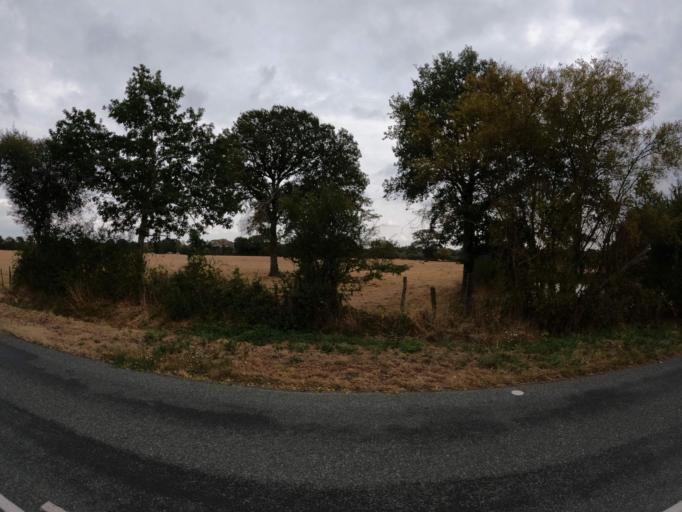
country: FR
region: Pays de la Loire
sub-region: Departement de Maine-et-Loire
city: Le Longeron
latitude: 47.0323
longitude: -1.0430
